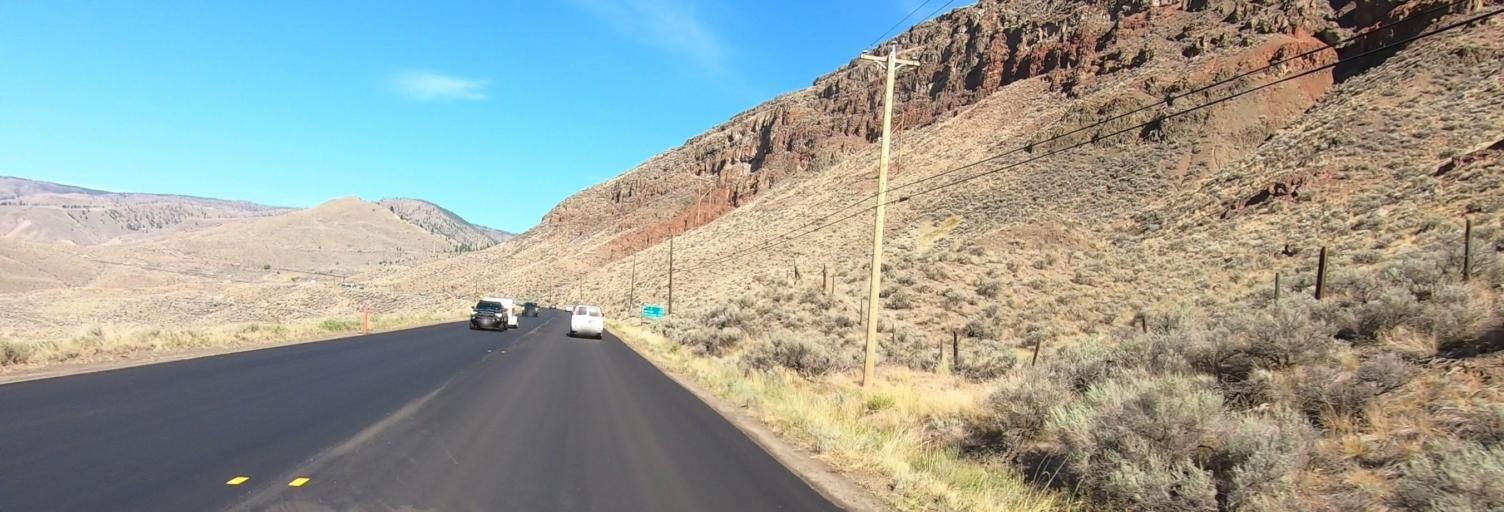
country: CA
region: British Columbia
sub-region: Thompson-Nicola Regional District
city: Ashcroft
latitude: 50.7931
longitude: -121.0886
